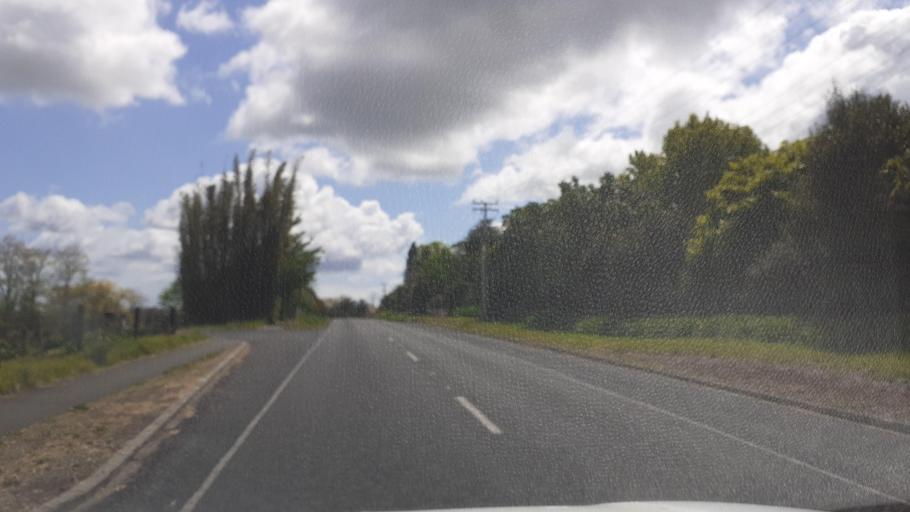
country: NZ
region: Northland
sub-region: Far North District
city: Kerikeri
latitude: -35.2201
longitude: 173.9781
